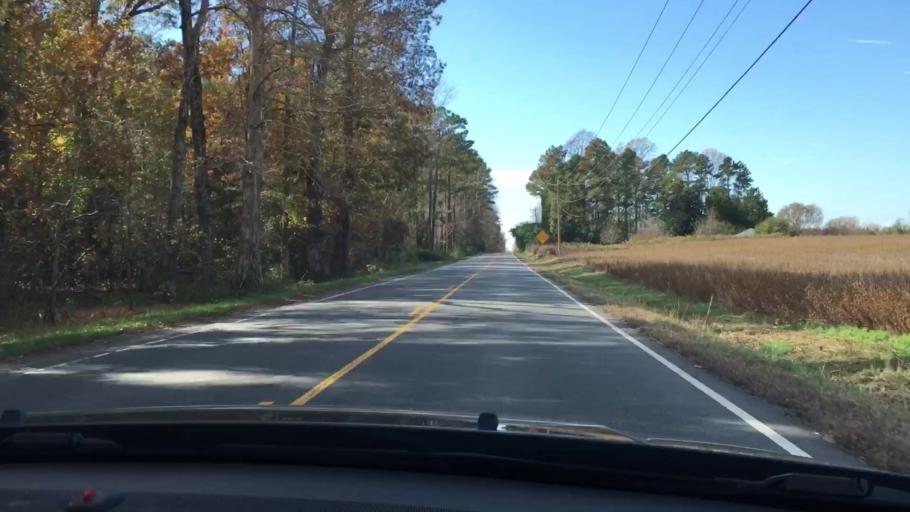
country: US
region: Virginia
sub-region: King and Queen County
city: King and Queen Court House
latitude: 37.5914
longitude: -76.8657
